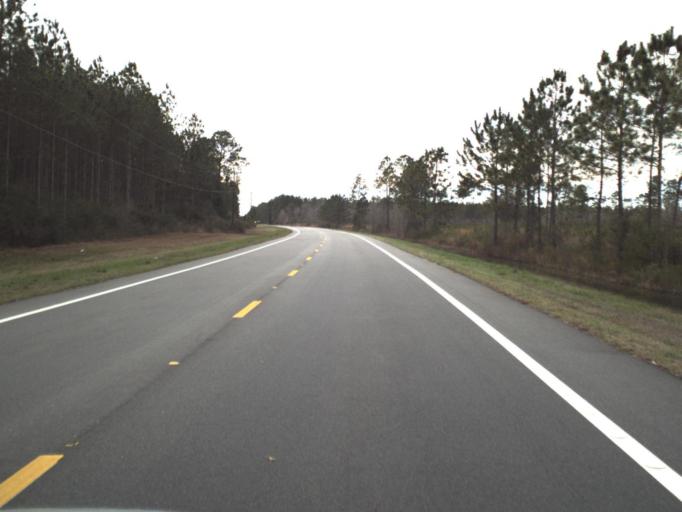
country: US
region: Florida
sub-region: Gulf County
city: Wewahitchka
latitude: 30.1384
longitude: -85.2481
